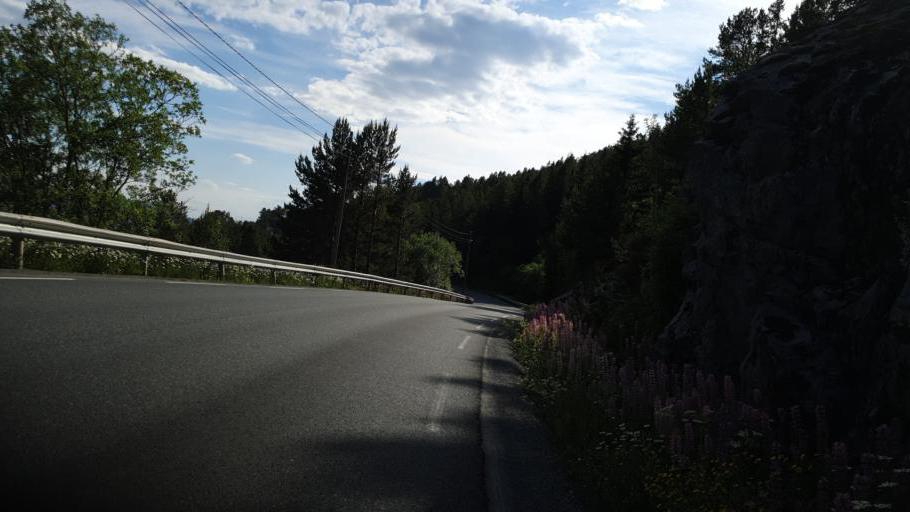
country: NO
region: Sor-Trondelag
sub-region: Trondheim
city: Trondheim
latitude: 63.5707
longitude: 10.3457
